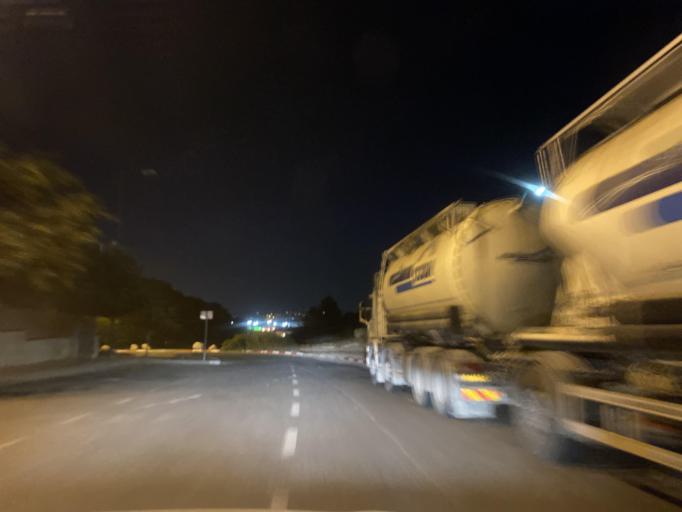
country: IL
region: Haifa
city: Daliyat el Karmil
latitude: 32.6409
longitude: 35.0894
